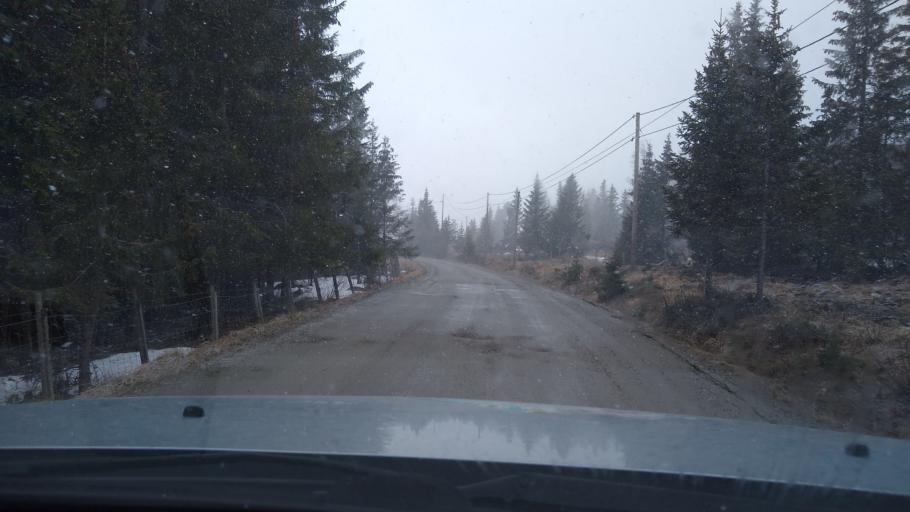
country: NO
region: Oppland
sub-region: Oyer
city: Tretten
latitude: 61.4621
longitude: 10.3424
